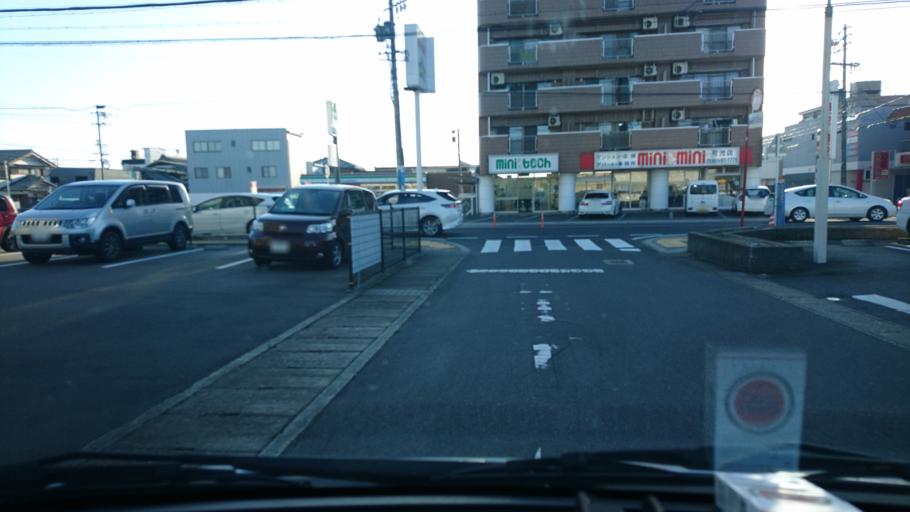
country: JP
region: Gifu
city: Mitake
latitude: 35.4233
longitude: 137.0632
